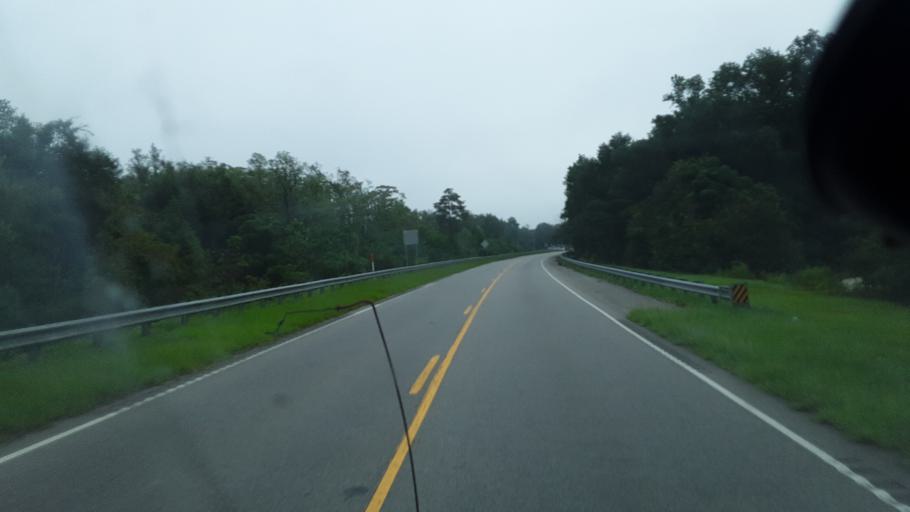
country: US
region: South Carolina
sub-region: Florence County
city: Johnsonville
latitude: 33.9119
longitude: -79.4237
